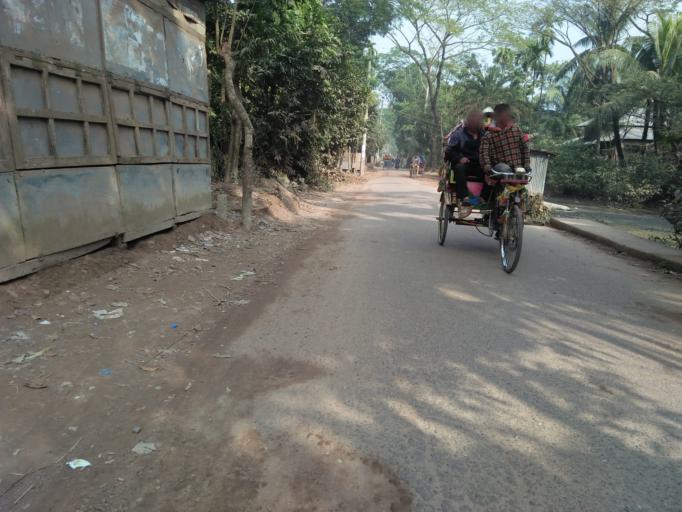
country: BD
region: Barisal
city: Bhola
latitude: 22.6773
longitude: 90.6365
